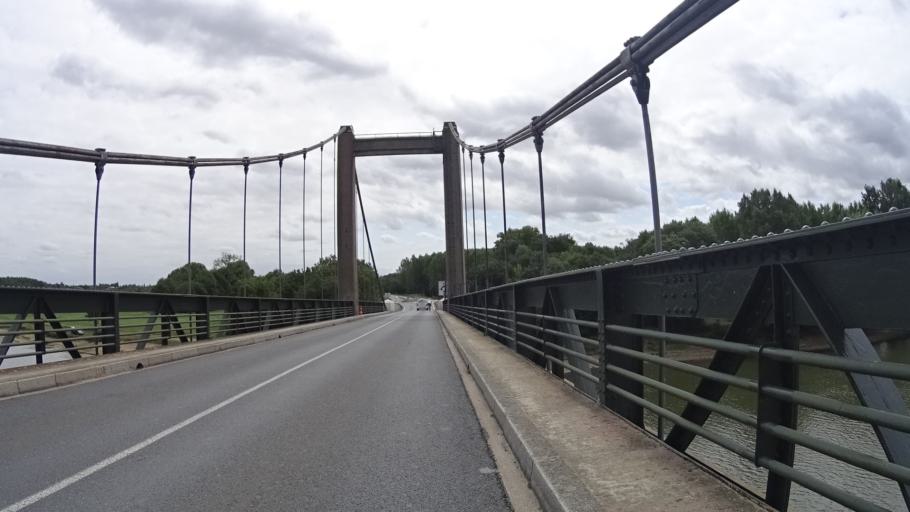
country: FR
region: Pays de la Loire
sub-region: Departement de Maine-et-Loire
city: Bouchemaine
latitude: 47.4204
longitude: -0.6084
